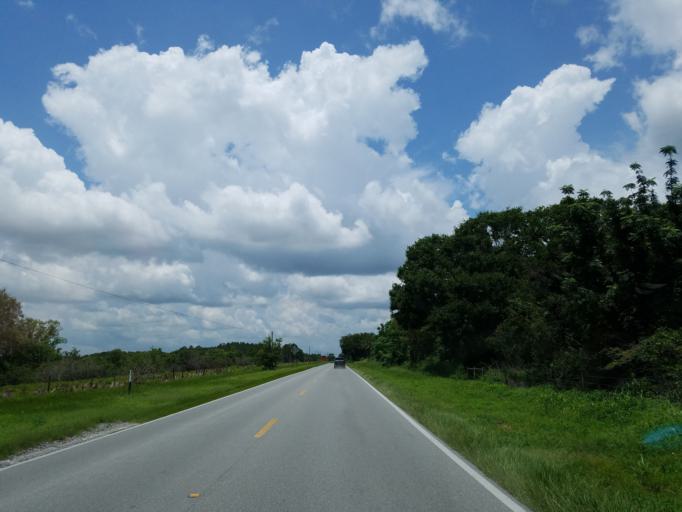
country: US
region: Florida
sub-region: Polk County
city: Mulberry
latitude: 27.8509
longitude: -81.9929
